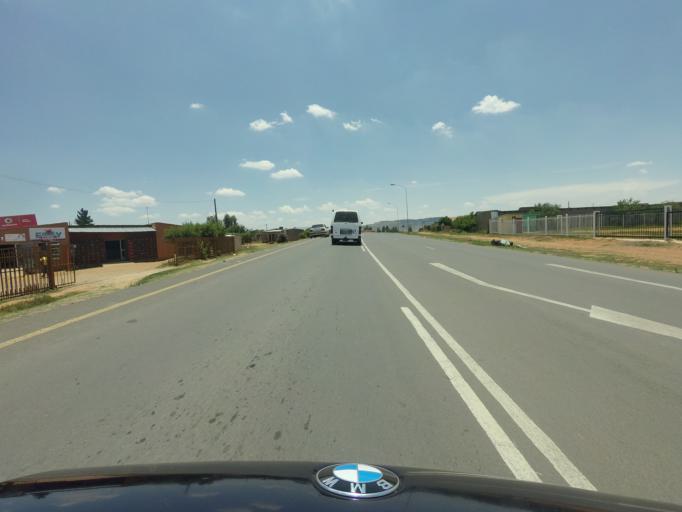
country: LS
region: Maseru
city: Maseru
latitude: -29.2748
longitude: 27.5298
